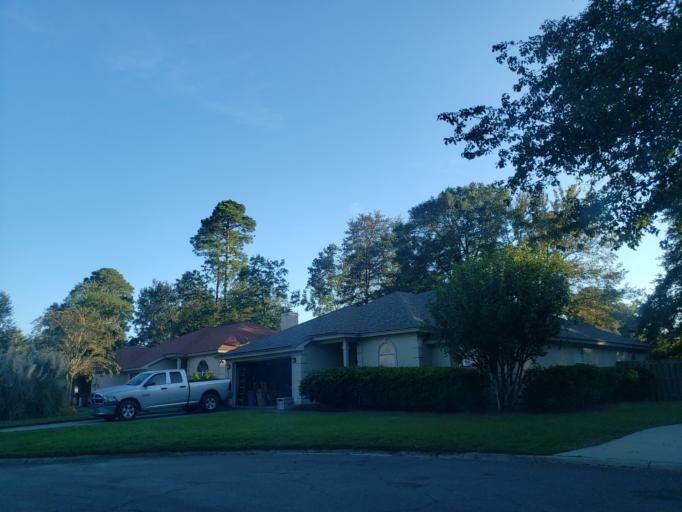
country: US
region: Georgia
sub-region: Chatham County
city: Isle of Hope
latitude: 31.9906
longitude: -81.0722
